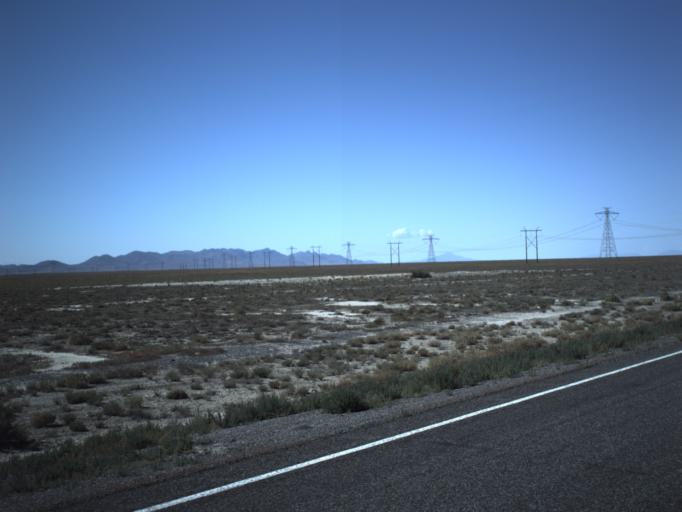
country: US
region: Utah
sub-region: Millard County
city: Delta
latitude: 39.2483
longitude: -112.9010
